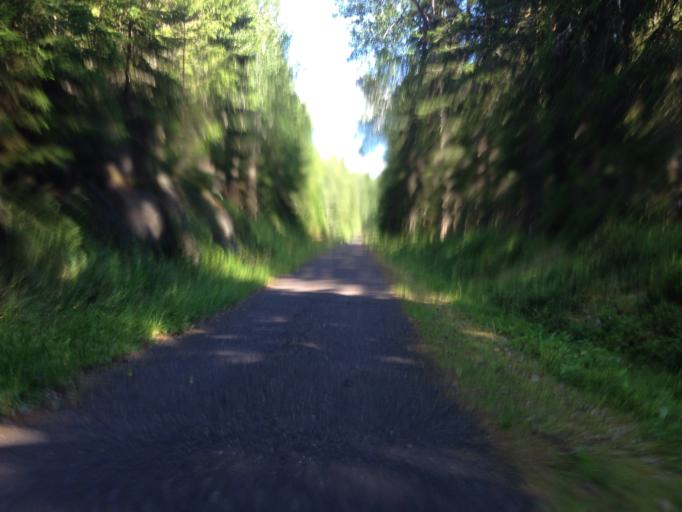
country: SE
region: Dalarna
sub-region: Ludvika Kommun
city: Ludvika
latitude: 60.2003
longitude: 15.0764
